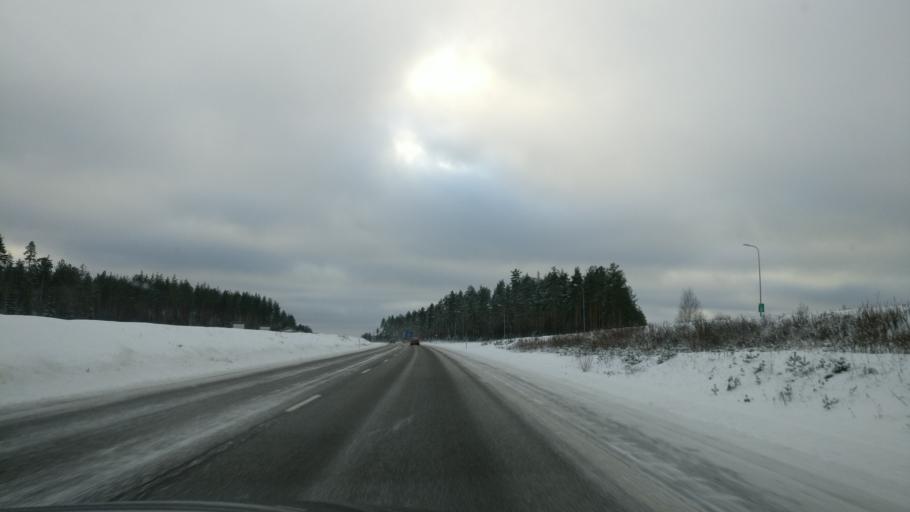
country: FI
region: Paijanne Tavastia
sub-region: Lahti
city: Heinola
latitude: 61.1130
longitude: 25.9227
